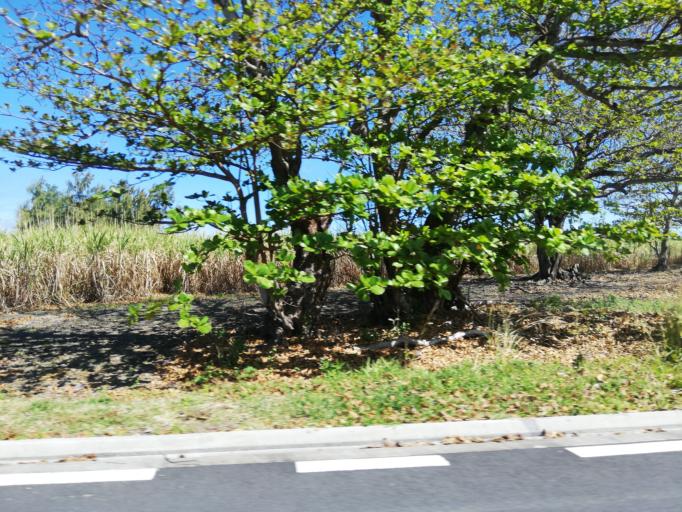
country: MU
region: Grand Port
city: Beau Vallon
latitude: -20.4521
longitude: 57.6977
